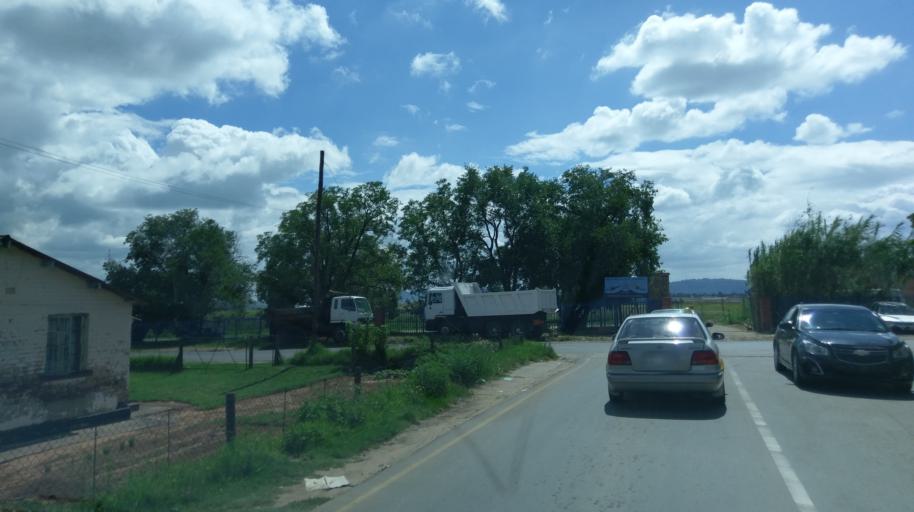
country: LS
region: Maseru
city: Maseru
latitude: -29.3094
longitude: 27.4989
